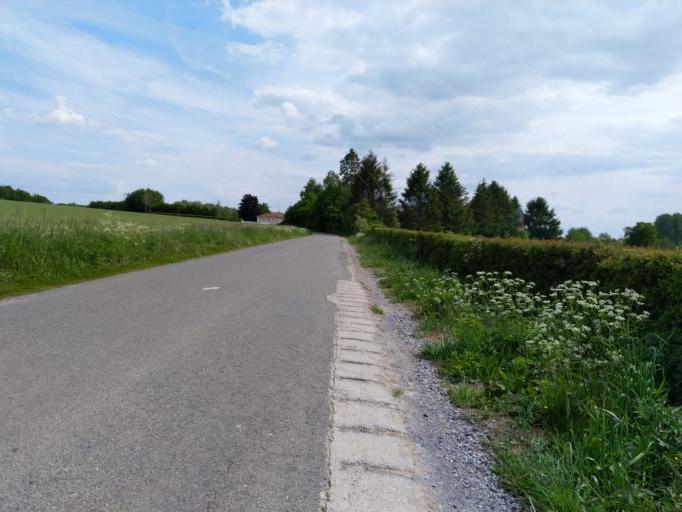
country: FR
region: Picardie
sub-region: Departement de l'Aisne
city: Boue
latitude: 50.0233
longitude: 3.6872
